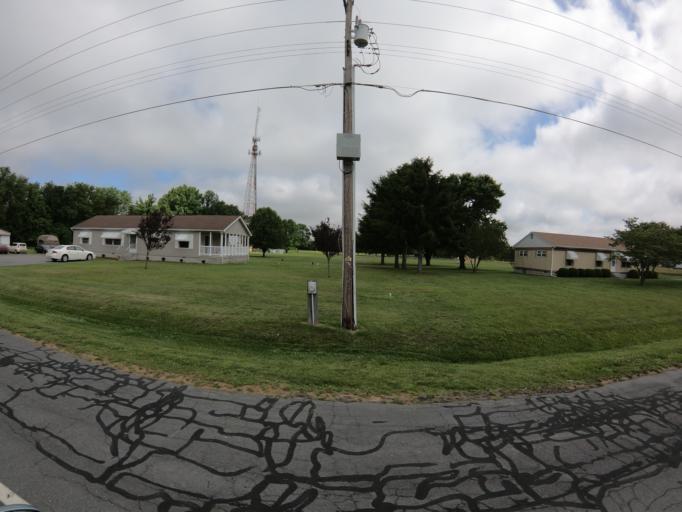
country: US
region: Delaware
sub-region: Kent County
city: Riverview
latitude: 39.0115
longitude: -75.5074
